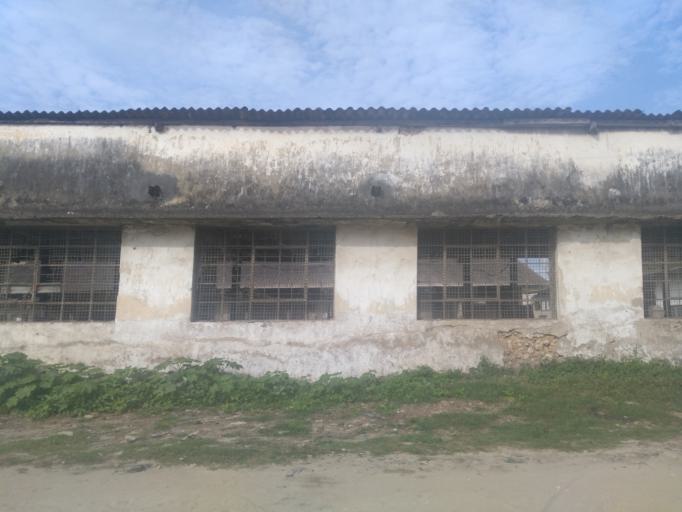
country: TZ
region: Zanzibar Urban/West
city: Zanzibar
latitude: -6.1576
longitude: 39.2091
